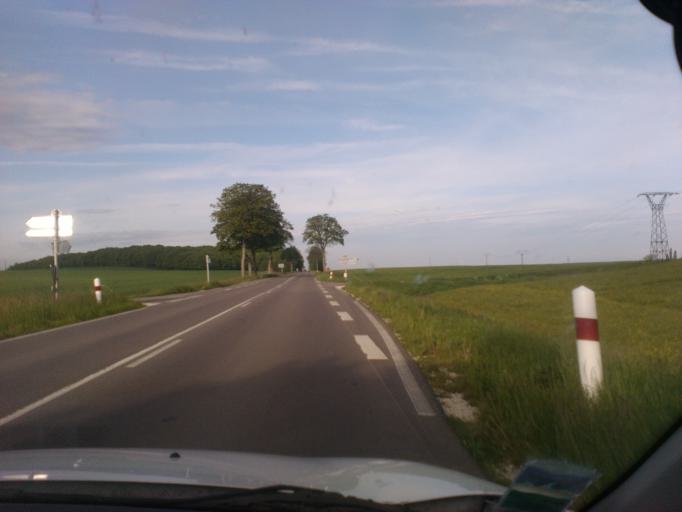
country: FR
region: Champagne-Ardenne
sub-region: Departement de l'Aube
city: Vendeuvre-sur-Barse
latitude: 48.2569
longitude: 4.5838
